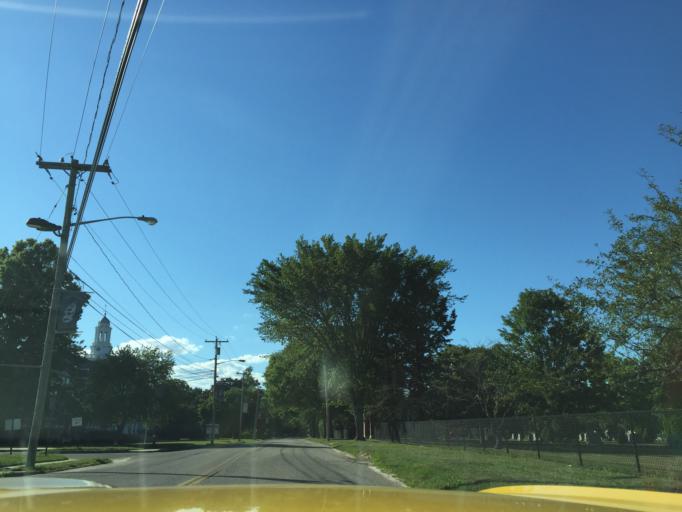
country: US
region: New York
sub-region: Suffolk County
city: Southold
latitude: 41.0605
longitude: -72.4308
